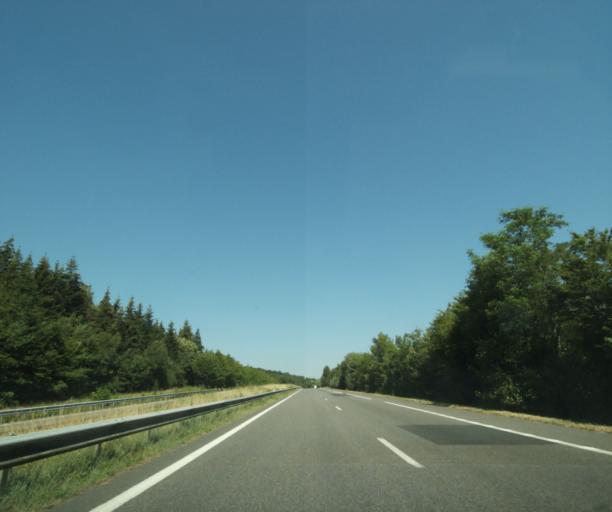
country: FR
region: Lorraine
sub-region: Departement de la Meuse
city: Vacon
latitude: 48.6887
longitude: 5.5578
